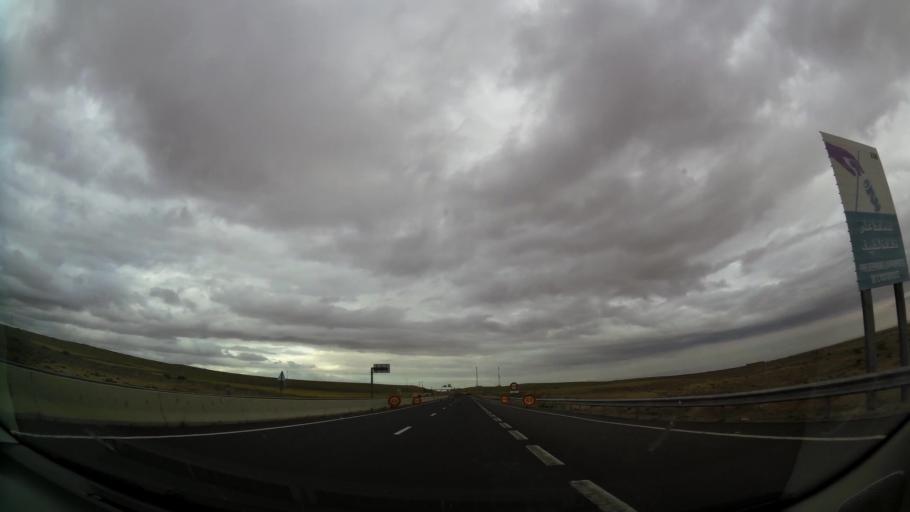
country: MA
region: Taza-Al Hoceima-Taounate
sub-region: Taza
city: Taza
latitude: 34.3082
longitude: -3.7188
